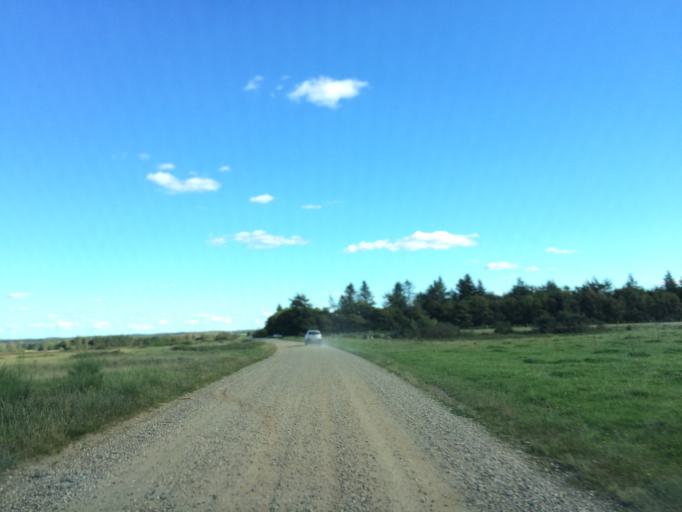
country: DK
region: Central Jutland
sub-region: Holstebro Kommune
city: Holstebro
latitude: 56.2761
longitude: 8.4928
